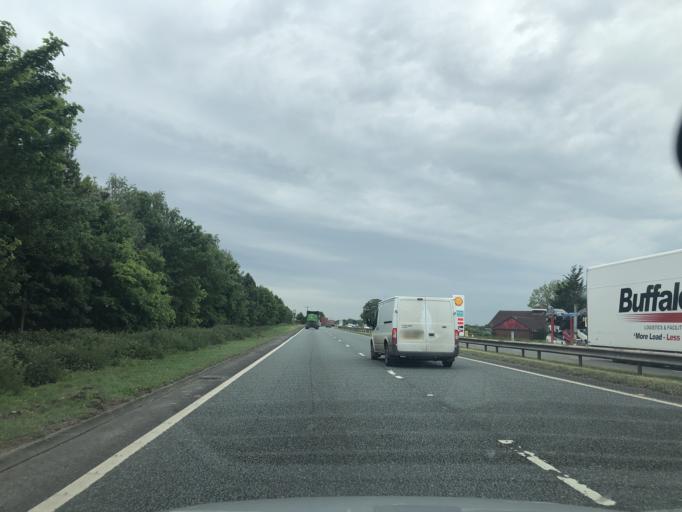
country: GB
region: England
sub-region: North Yorkshire
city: Thirsk
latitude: 54.1980
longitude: -1.3617
